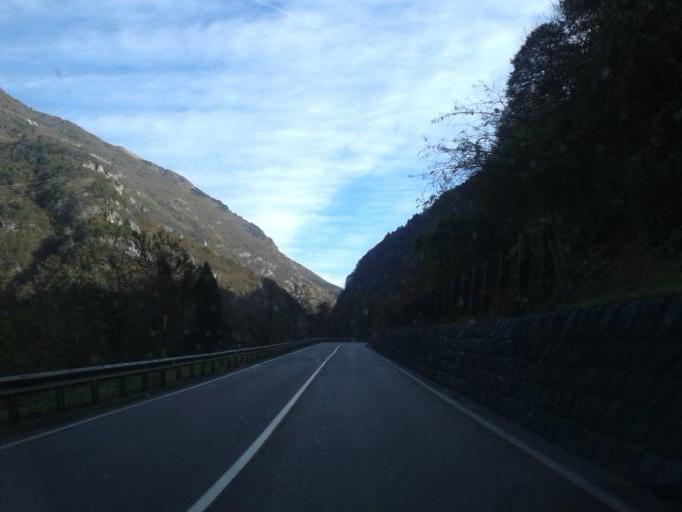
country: IT
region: Trentino-Alto Adige
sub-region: Provincia di Trento
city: Ragoli
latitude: 46.0525
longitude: 10.8076
